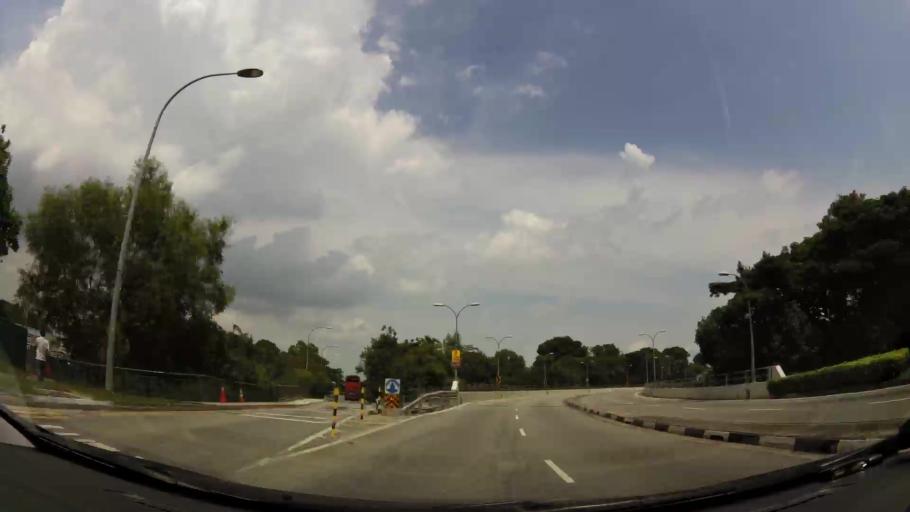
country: MY
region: Johor
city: Kampung Pasir Gudang Baru
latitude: 1.3898
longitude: 103.9903
